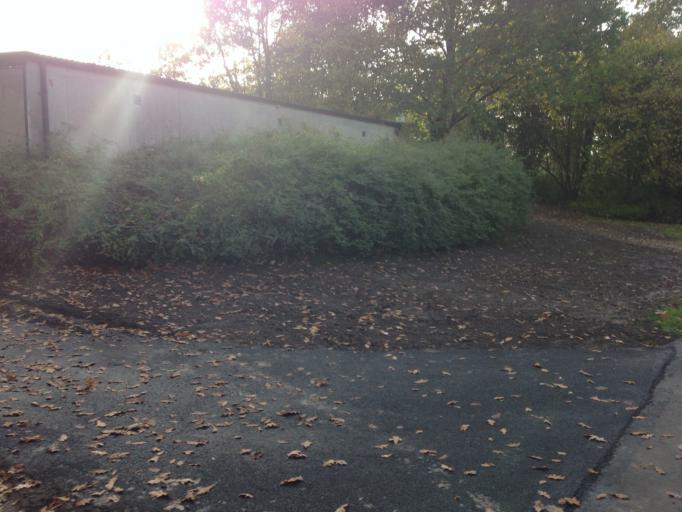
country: SE
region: Skane
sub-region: Lunds Kommun
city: Lund
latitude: 55.7232
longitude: 13.2151
